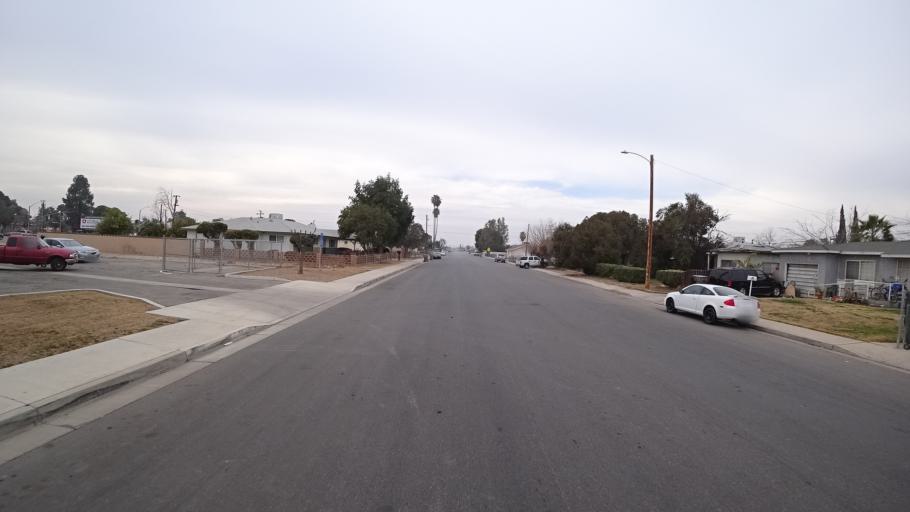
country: US
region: California
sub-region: Kern County
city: Bakersfield
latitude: 35.3692
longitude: -118.9896
